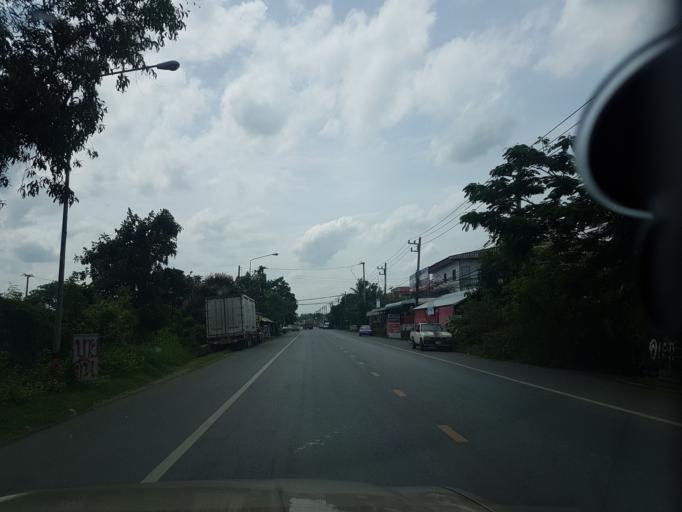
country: TH
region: Sara Buri
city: Nong Khae
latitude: 14.3275
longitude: 100.8782
